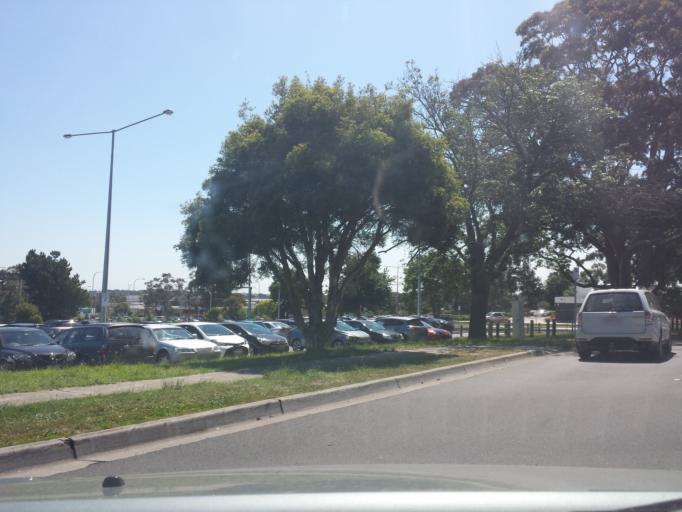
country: AU
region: Victoria
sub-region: Casey
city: Berwick
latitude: -38.0381
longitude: 145.3449
